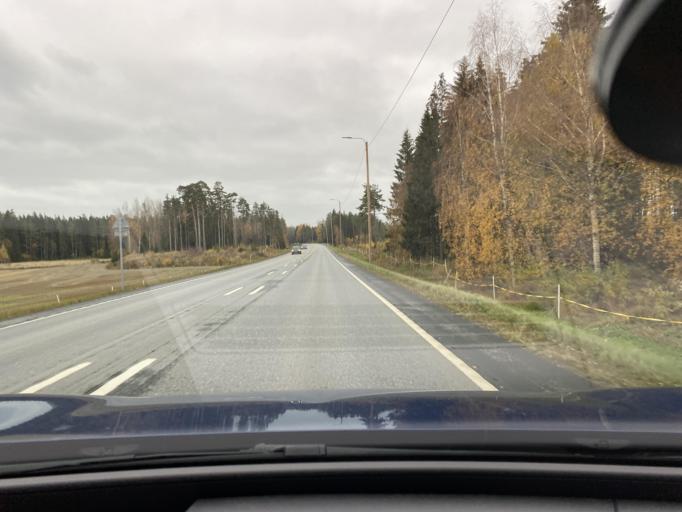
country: FI
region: Varsinais-Suomi
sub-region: Vakka-Suomi
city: Laitila
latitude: 60.9398
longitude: 21.6026
